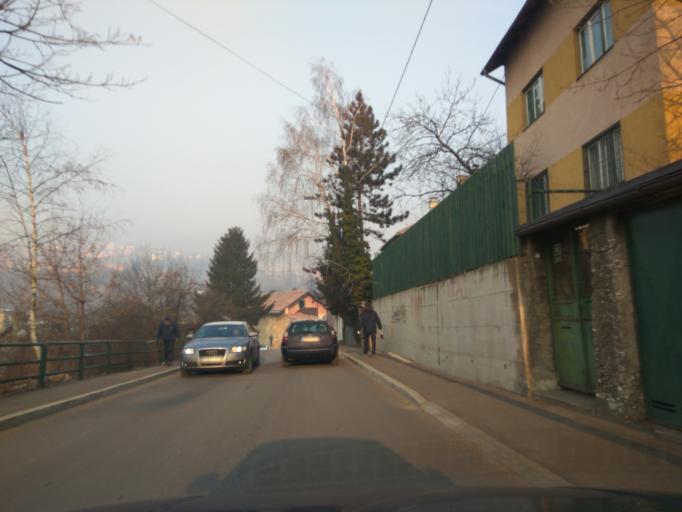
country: BA
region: Federation of Bosnia and Herzegovina
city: Kobilja Glava
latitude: 43.8598
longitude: 18.4018
